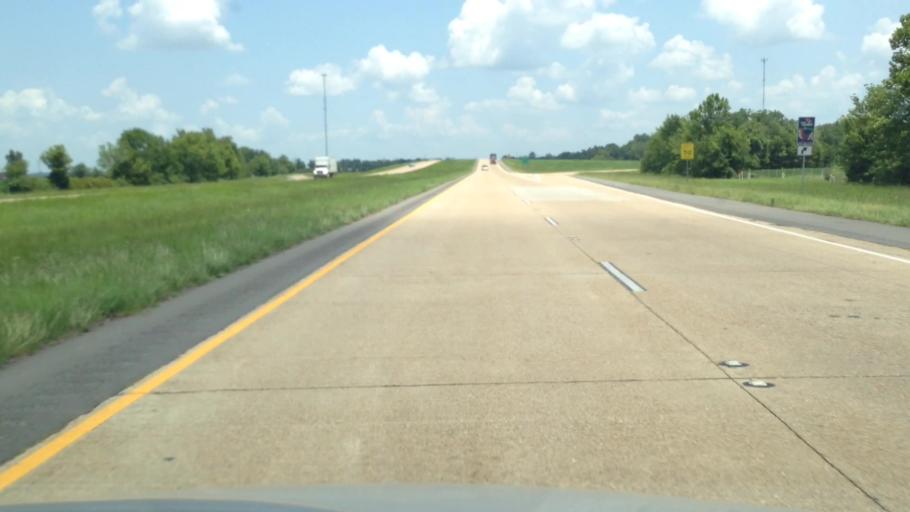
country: US
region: Louisiana
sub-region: Rapides Parish
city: Lecompte
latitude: 31.0168
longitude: -92.3819
